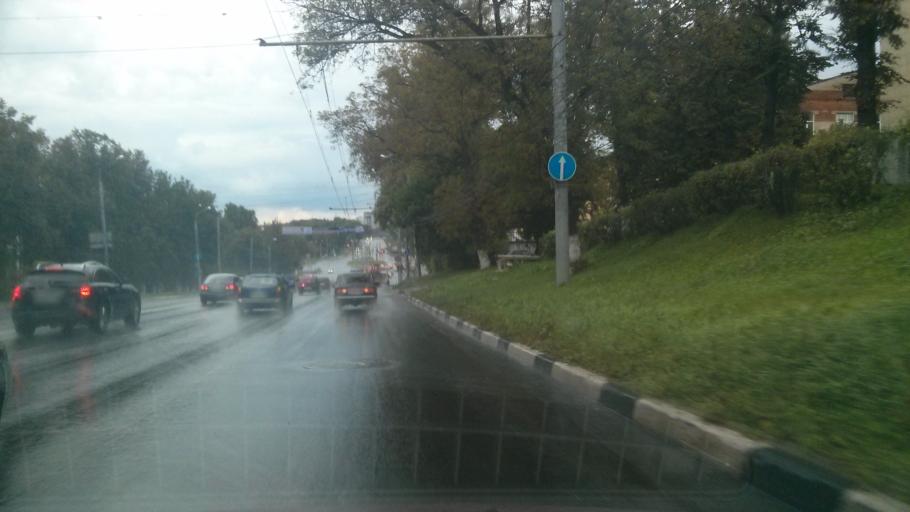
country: RU
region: Nizjnij Novgorod
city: Nizhniy Novgorod
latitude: 56.2518
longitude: 43.9686
